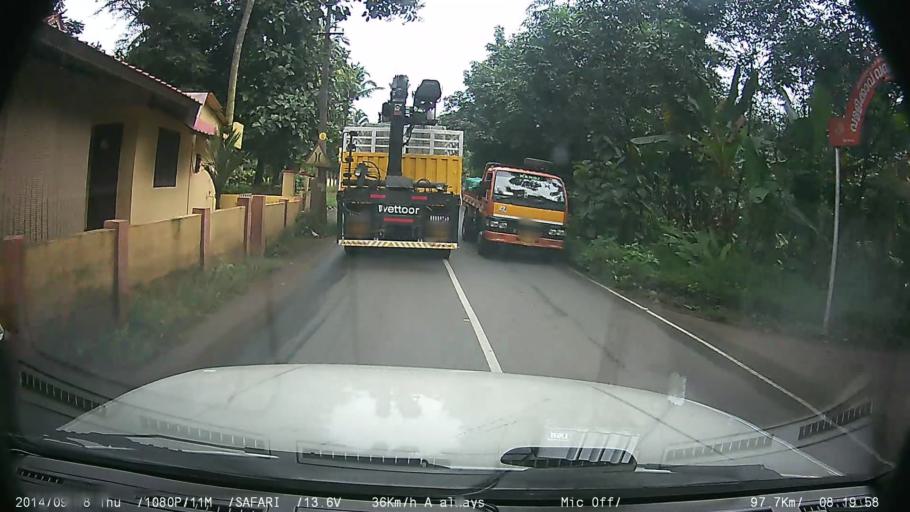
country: IN
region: Kerala
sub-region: Kottayam
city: Palackattumala
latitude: 9.6567
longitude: 76.6128
